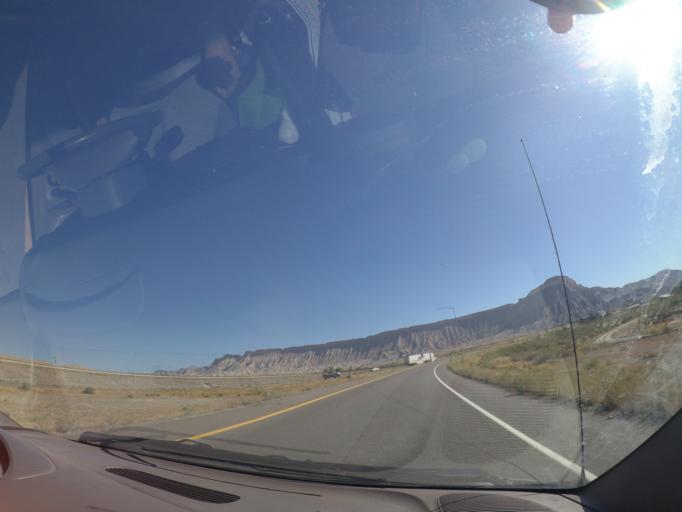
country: US
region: Colorado
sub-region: Mesa County
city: Clifton
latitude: 39.1037
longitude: -108.4457
